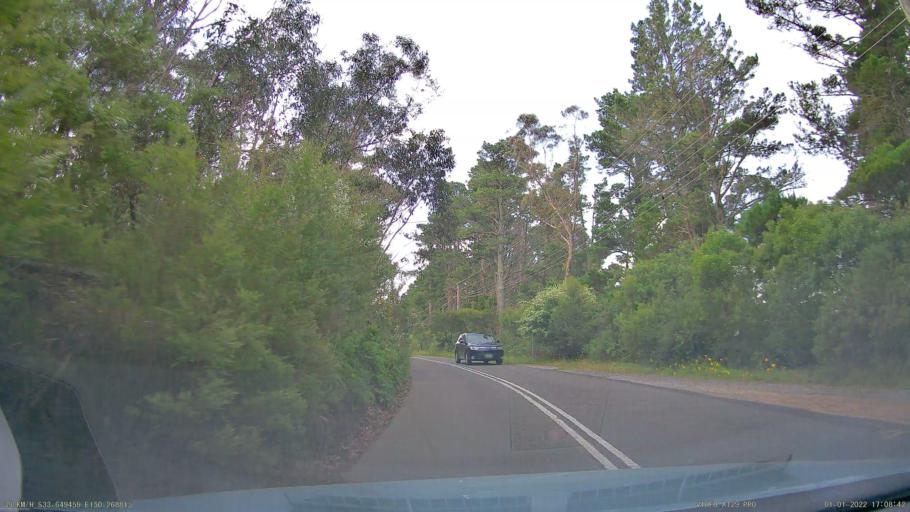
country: AU
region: New South Wales
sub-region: Blue Mountains Municipality
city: Blackheath
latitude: -33.6494
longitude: 150.2688
